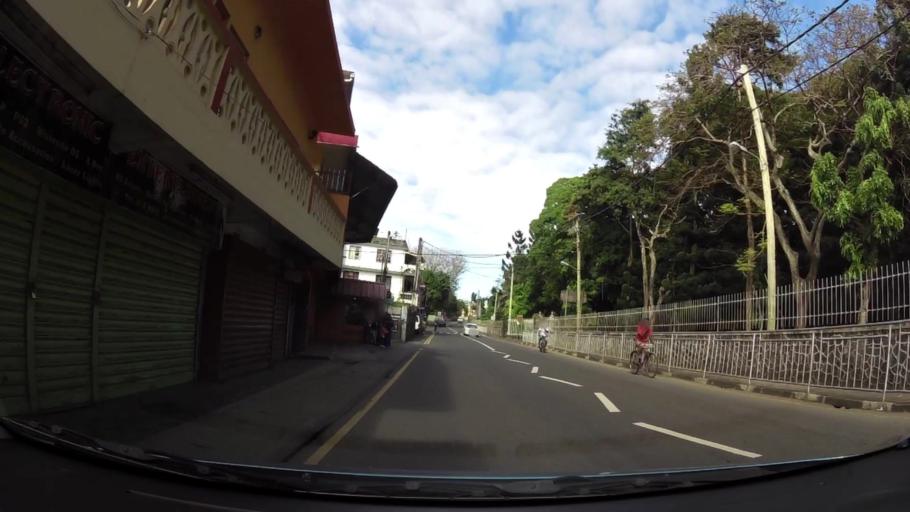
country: MU
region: Grand Port
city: Mahebourg
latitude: -20.4156
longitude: 57.7050
